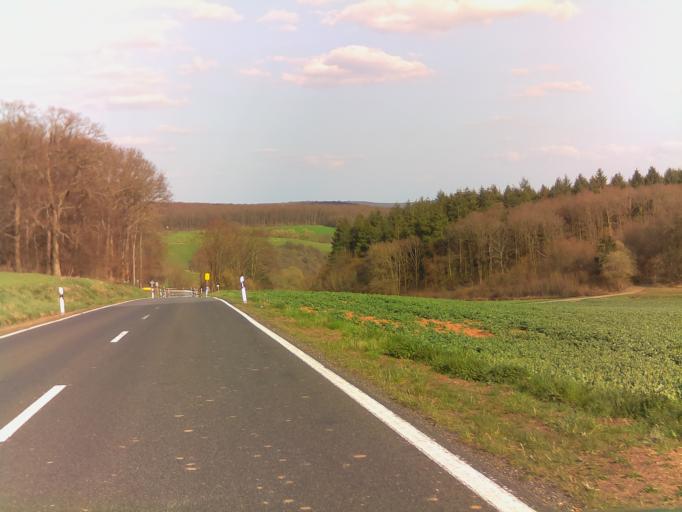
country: DE
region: Rheinland-Pfalz
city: Abtweiler
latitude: 49.7486
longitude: 7.6352
